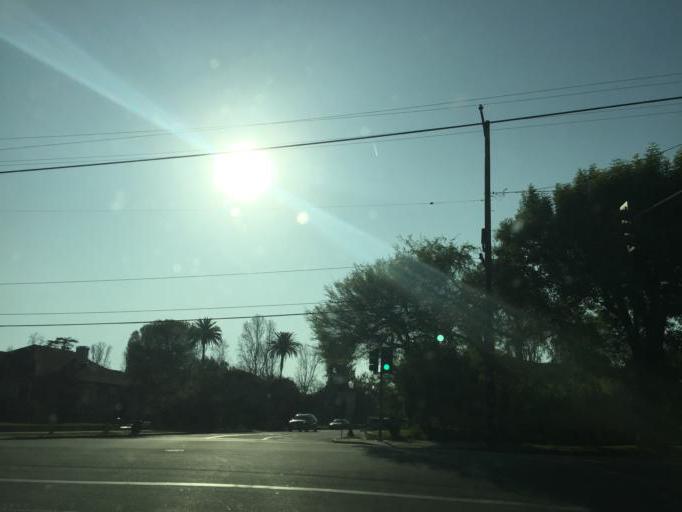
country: US
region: California
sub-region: Los Angeles County
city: South Pasadena
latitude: 34.1160
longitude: -118.1414
